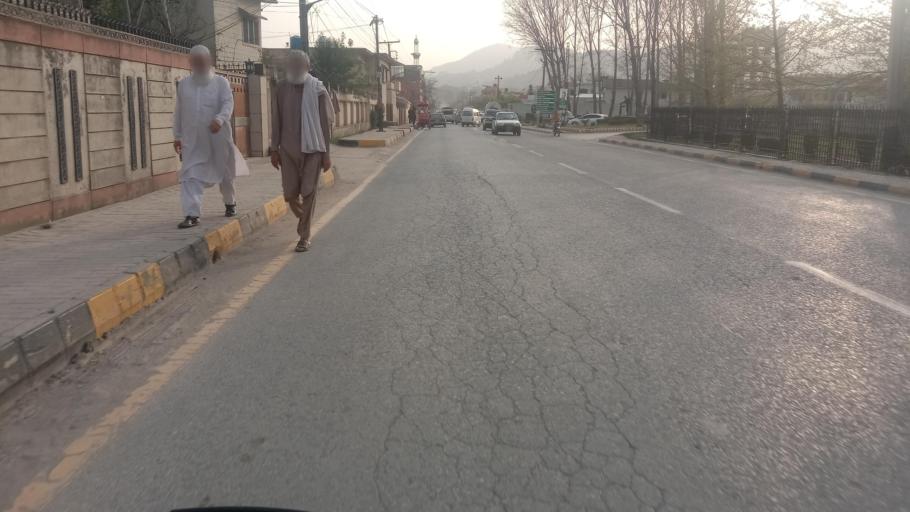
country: PK
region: Khyber Pakhtunkhwa
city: Abbottabad
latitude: 34.1721
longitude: 73.2354
